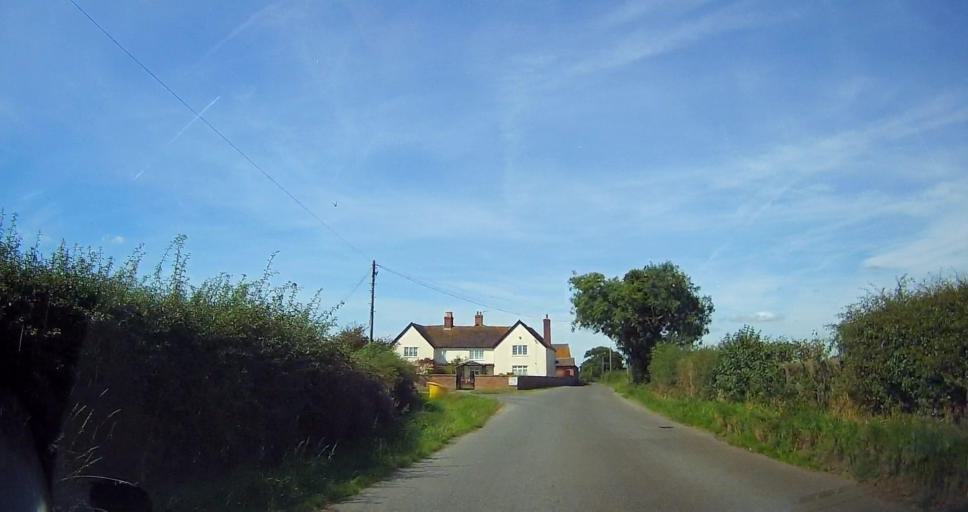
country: GB
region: England
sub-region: Cheshire East
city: Nantwich
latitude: 52.9875
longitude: -2.5331
